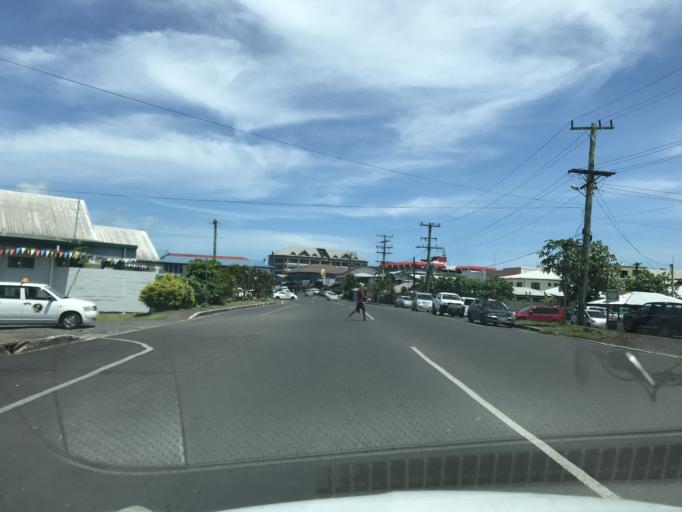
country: WS
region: Tuamasaga
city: Apia
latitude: -13.8327
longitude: -171.7671
